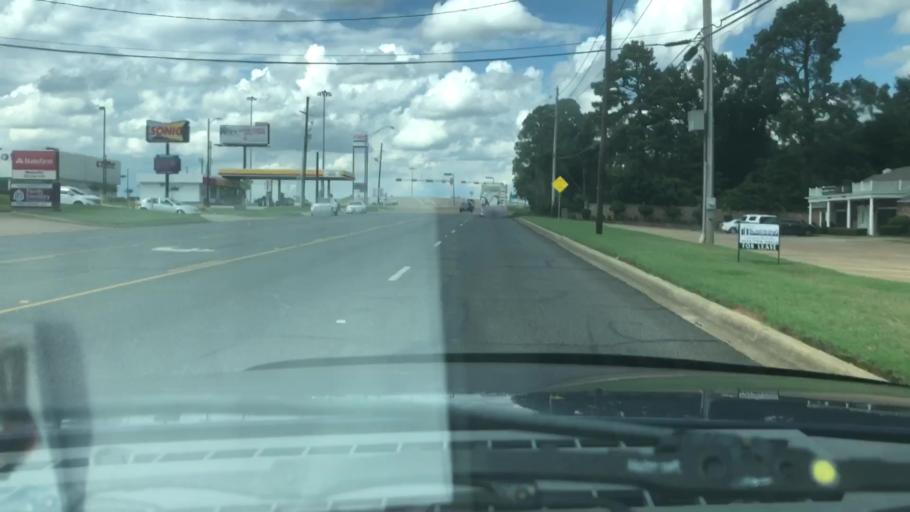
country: US
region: Arkansas
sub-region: Miller County
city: Texarkana
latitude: 33.4620
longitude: -94.0658
